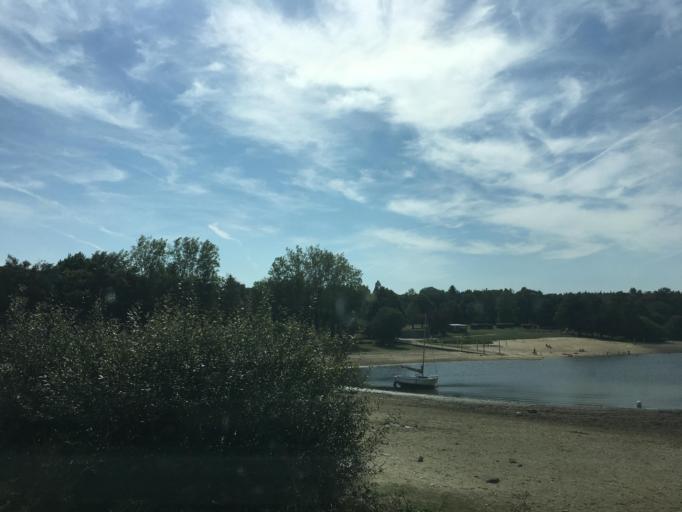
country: FR
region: Brittany
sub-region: Departement des Cotes-d'Armor
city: Mur-de-Bretagne
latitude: 48.2111
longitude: -3.0114
